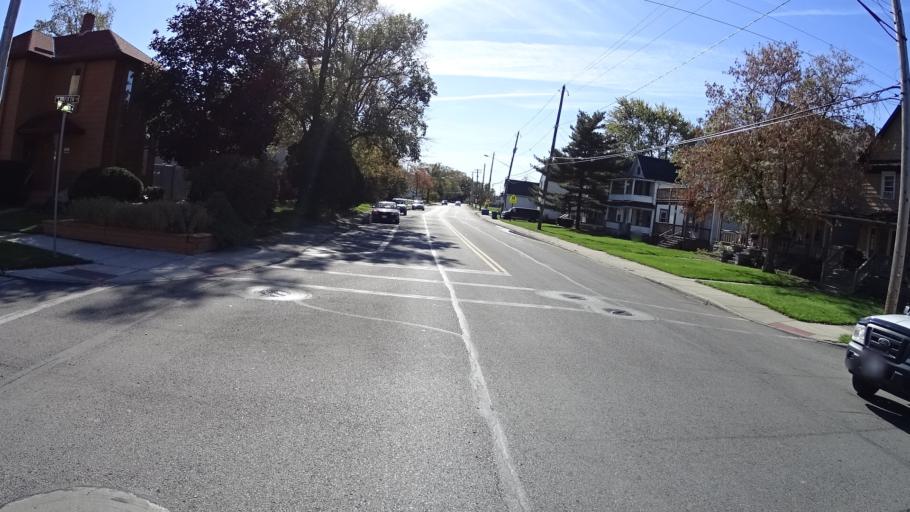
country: US
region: Ohio
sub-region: Lorain County
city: Lorain
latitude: 41.4656
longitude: -82.1798
